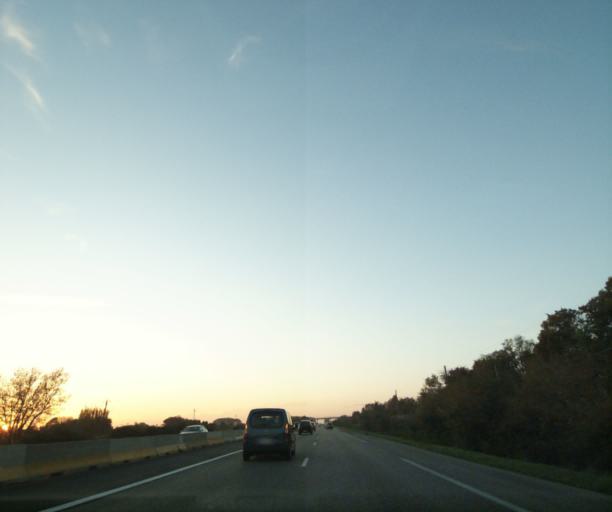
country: FR
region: Provence-Alpes-Cote d'Azur
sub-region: Departement des Bouches-du-Rhone
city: Arles
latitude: 43.6454
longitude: 4.6970
